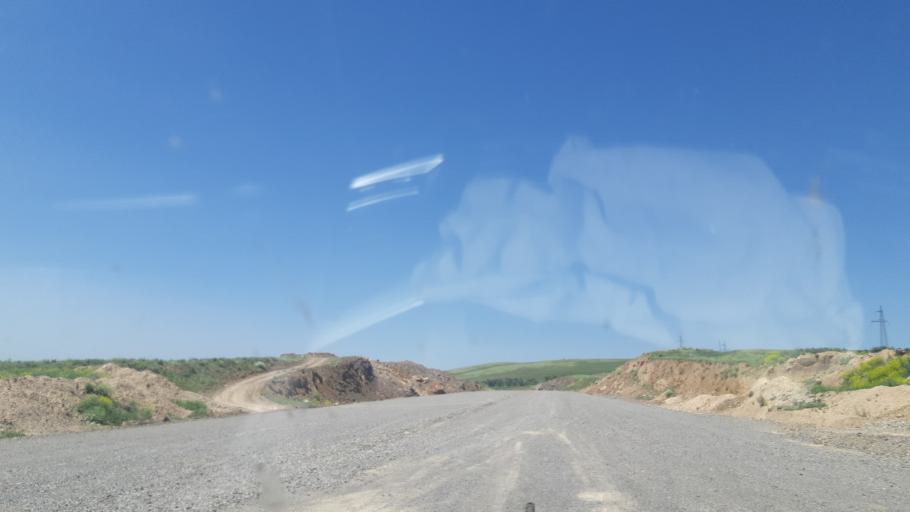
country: KZ
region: Ongtustik Qazaqstan
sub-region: Tulkibas Audany
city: Zhabagly
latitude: 42.5177
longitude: 70.5445
